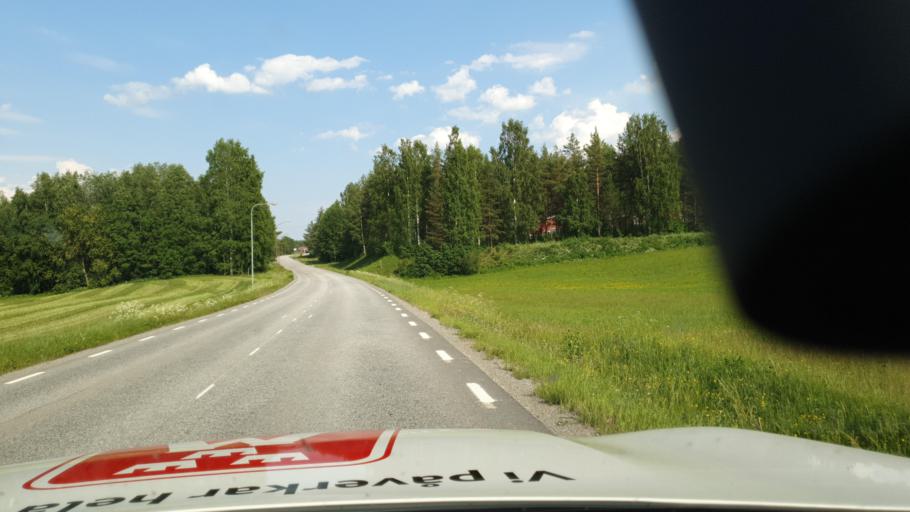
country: SE
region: Vaesterbotten
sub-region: Skelleftea Kommun
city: Viken
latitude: 64.7472
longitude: 20.8580
